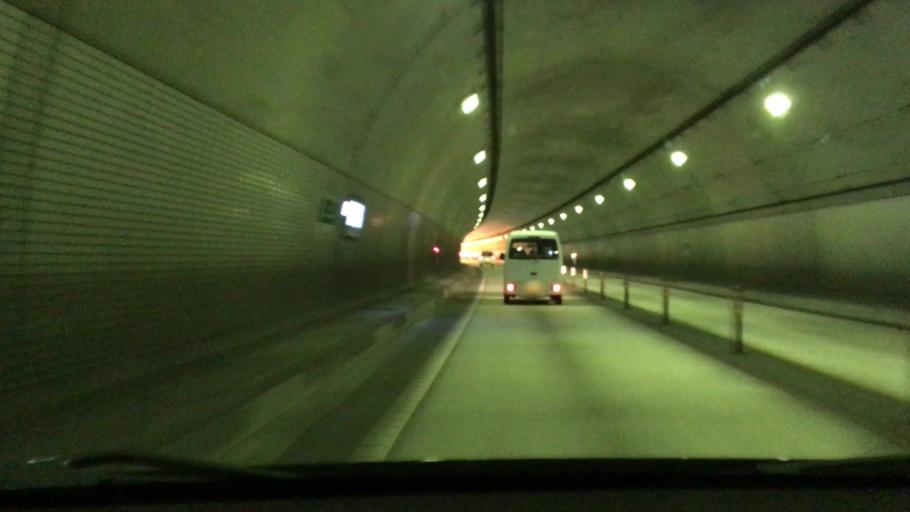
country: JP
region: Nagasaki
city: Sasebo
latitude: 33.0979
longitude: 129.7788
